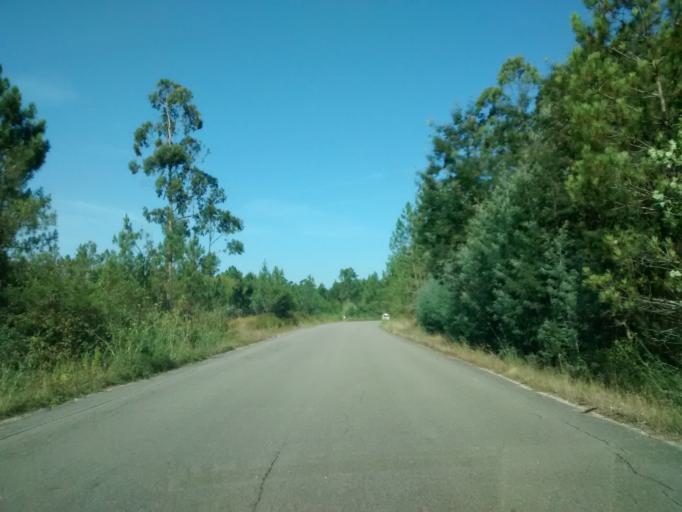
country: PT
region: Coimbra
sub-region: Cantanhede
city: Cantanhede
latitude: 40.4232
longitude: -8.6160
